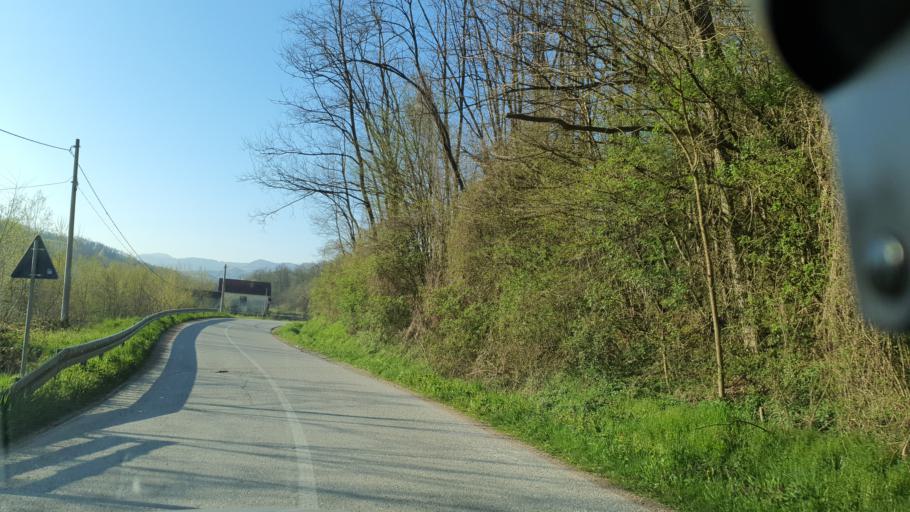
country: RS
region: Central Serbia
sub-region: Kolubarski Okrug
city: Osecina
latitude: 44.3136
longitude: 19.5264
